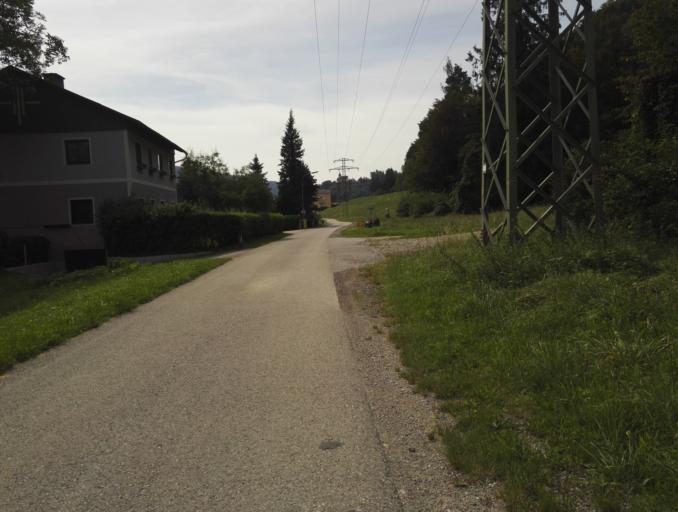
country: AT
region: Styria
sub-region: Politischer Bezirk Graz-Umgebung
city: Peggau
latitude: 47.2130
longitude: 15.3357
